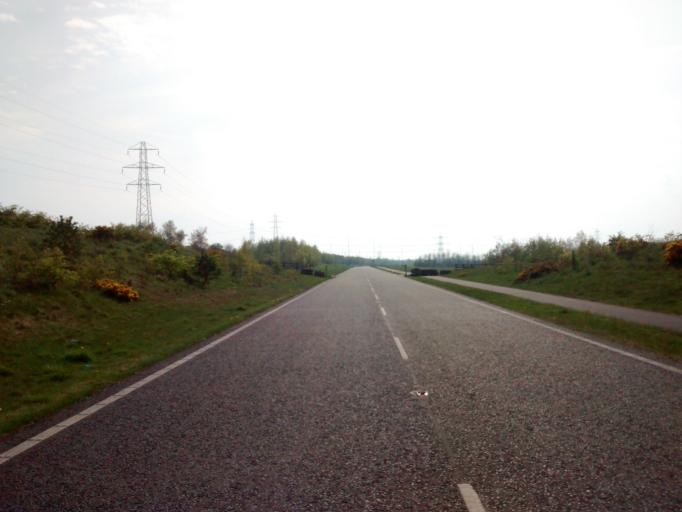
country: GB
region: England
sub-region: County Durham
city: South Hetton
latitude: 54.8067
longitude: -1.3828
